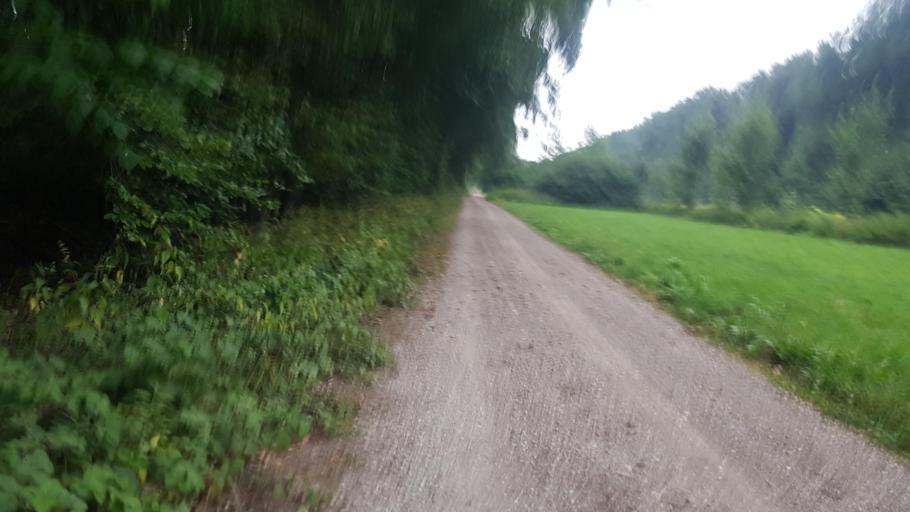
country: DE
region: Bavaria
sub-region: Upper Bavaria
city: Gauting
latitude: 48.0401
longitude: 11.3581
